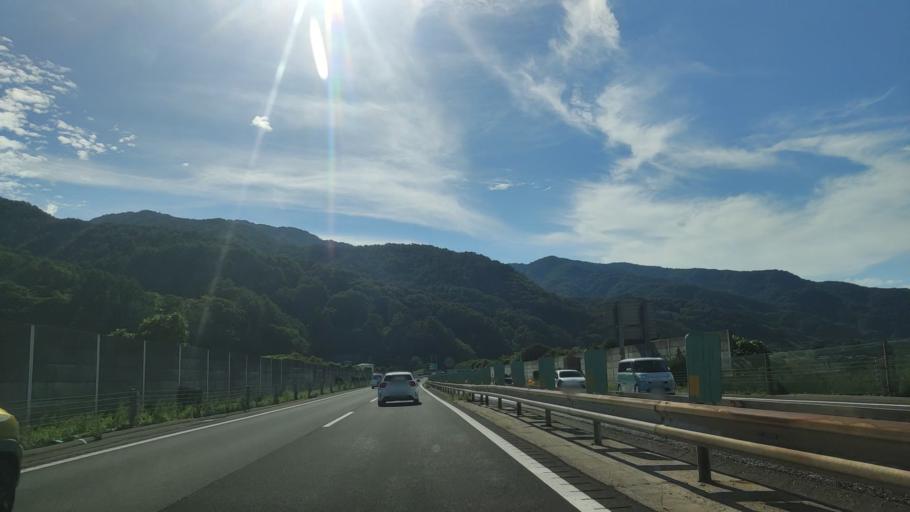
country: JP
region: Nagano
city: Suwa
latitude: 36.0033
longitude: 138.1164
